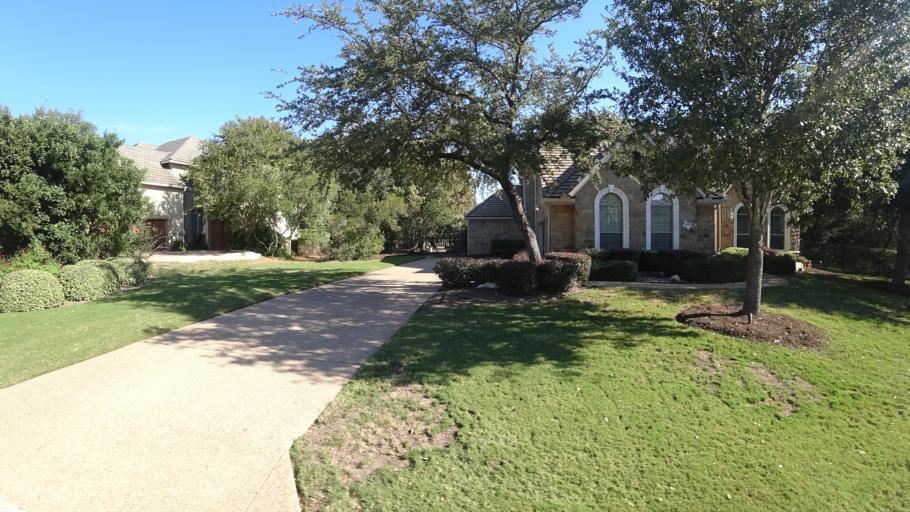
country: US
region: Texas
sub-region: Travis County
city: Barton Creek
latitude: 30.3538
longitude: -97.8859
